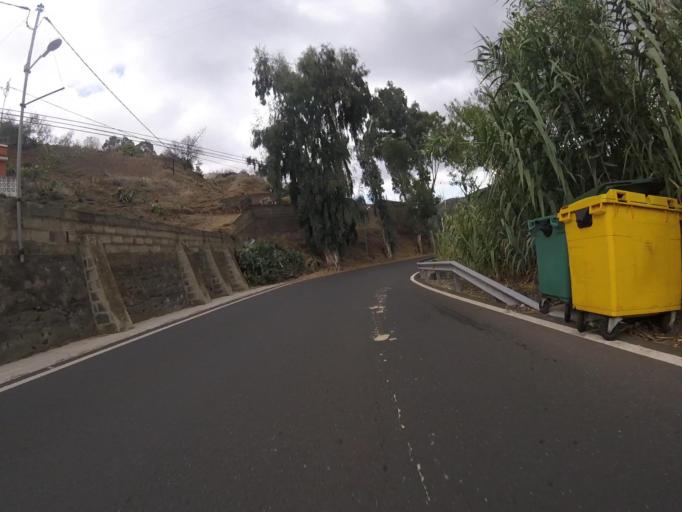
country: ES
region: Canary Islands
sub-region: Provincia de Las Palmas
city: Vega de San Mateo
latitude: 28.0071
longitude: -15.5407
